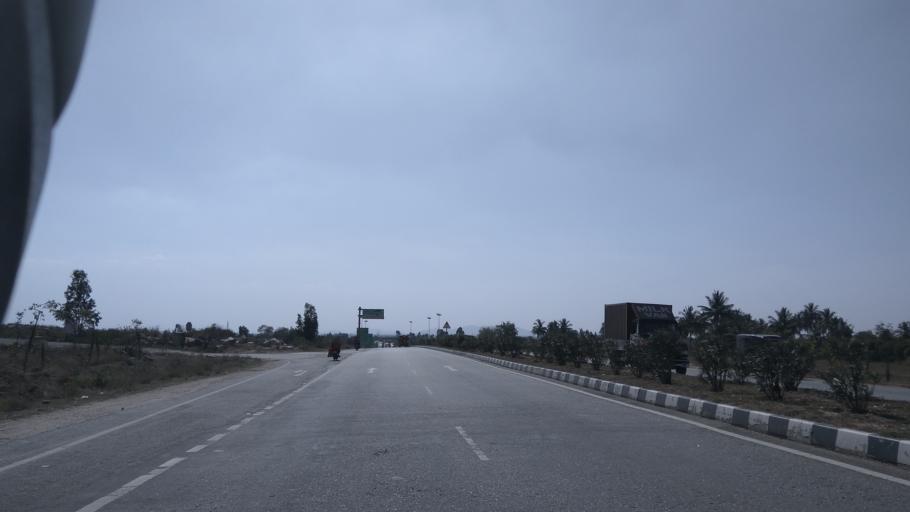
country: IN
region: Karnataka
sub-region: Kolar
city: Mulbagal
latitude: 13.1496
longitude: 78.2969
